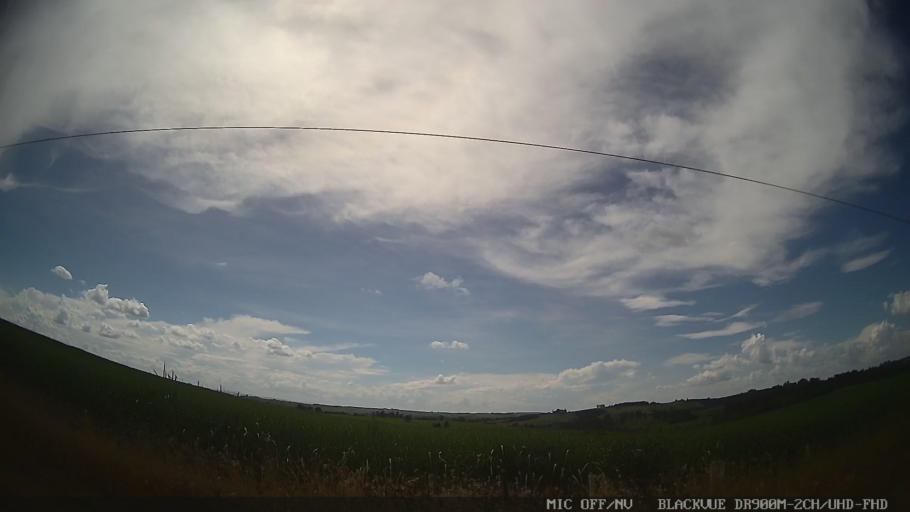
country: BR
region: Sao Paulo
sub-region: Conchas
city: Conchas
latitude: -22.9734
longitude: -47.9865
